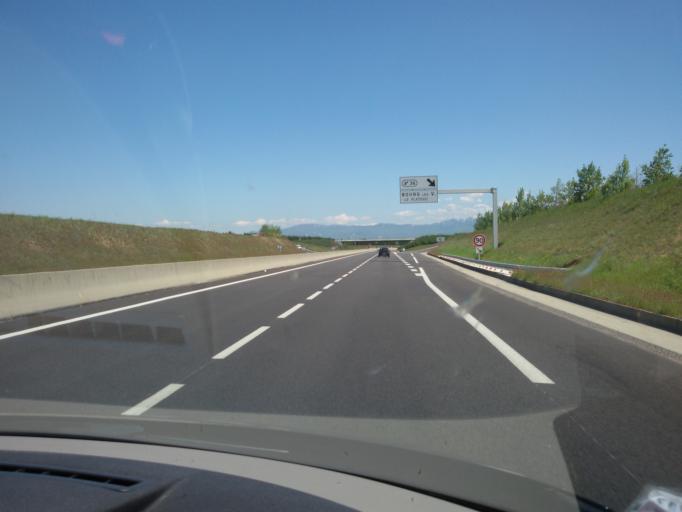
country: FR
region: Rhone-Alpes
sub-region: Departement de la Drome
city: Bourg-les-Valence
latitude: 44.9651
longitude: 4.9055
